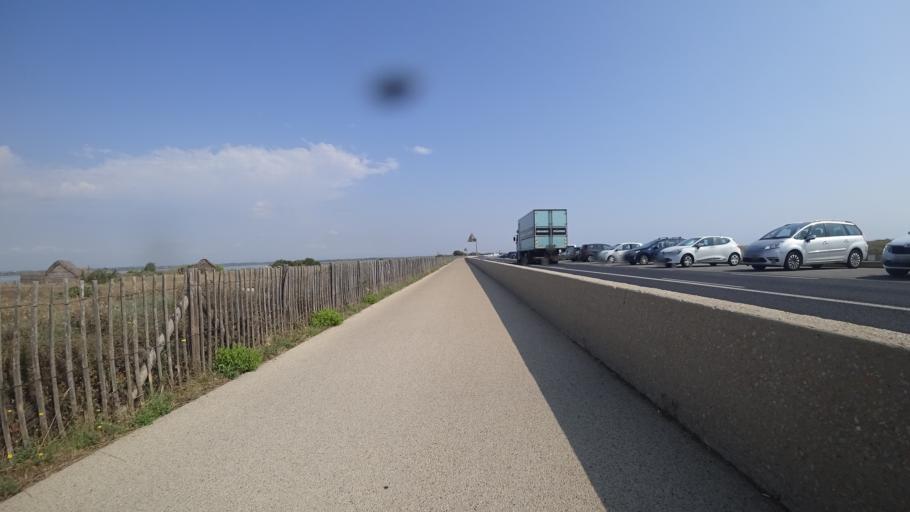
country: FR
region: Languedoc-Roussillon
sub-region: Departement des Pyrenees-Orientales
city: Saint-Cyprien-Plage
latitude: 42.6604
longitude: 3.0326
